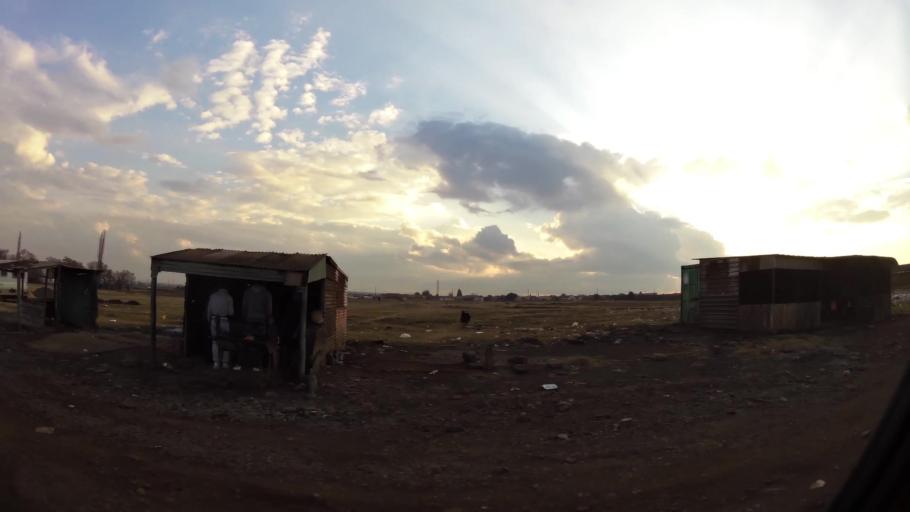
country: ZA
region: Gauteng
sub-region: City of Johannesburg Metropolitan Municipality
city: Orange Farm
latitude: -26.5397
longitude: 27.8325
